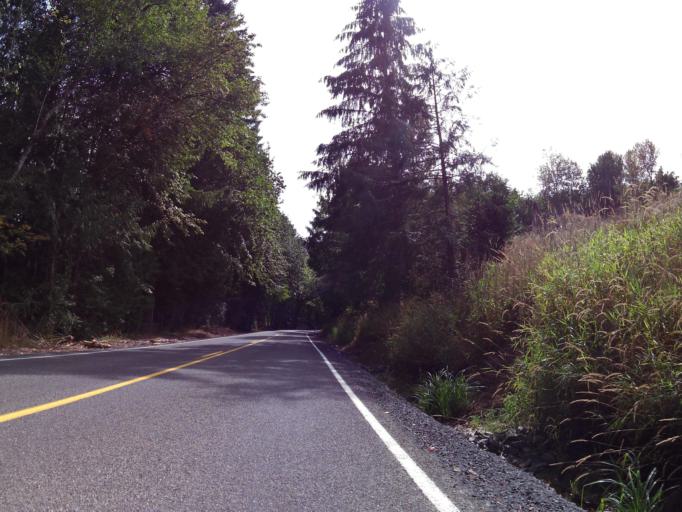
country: US
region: Washington
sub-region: Lewis County
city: Napavine
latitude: 46.5580
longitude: -122.9598
